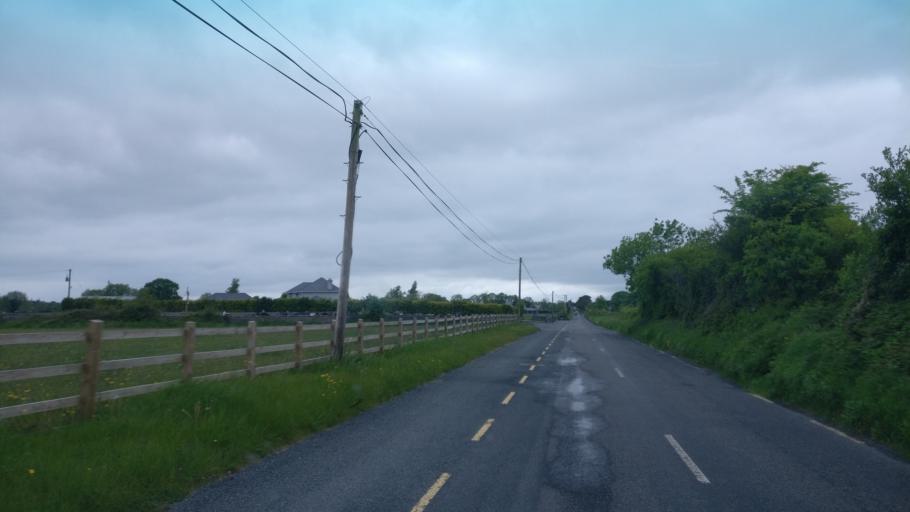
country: IE
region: Connaught
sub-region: County Galway
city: Portumna
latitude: 53.0922
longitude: -8.2350
